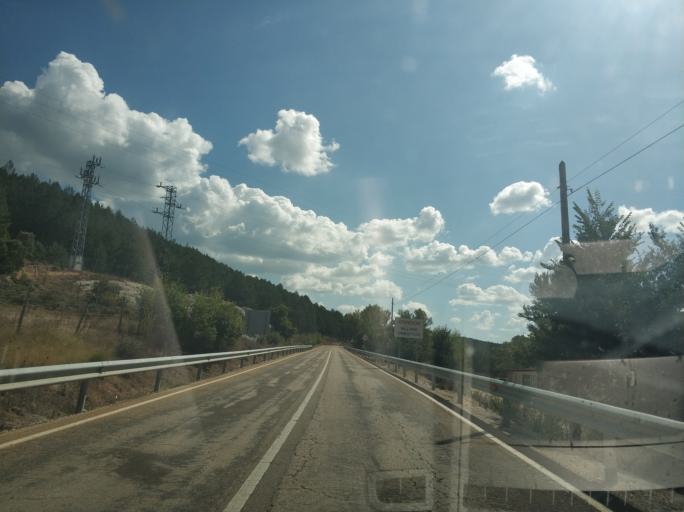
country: ES
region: Castille and Leon
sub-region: Provincia de Soria
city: San Leonardo de Yague
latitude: 41.8221
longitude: -3.0716
